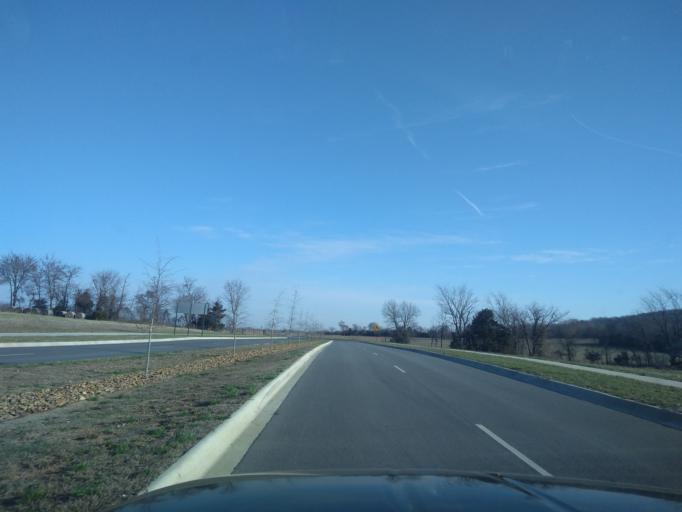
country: US
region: Arkansas
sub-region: Washington County
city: Farmington
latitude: 36.0523
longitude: -94.2199
